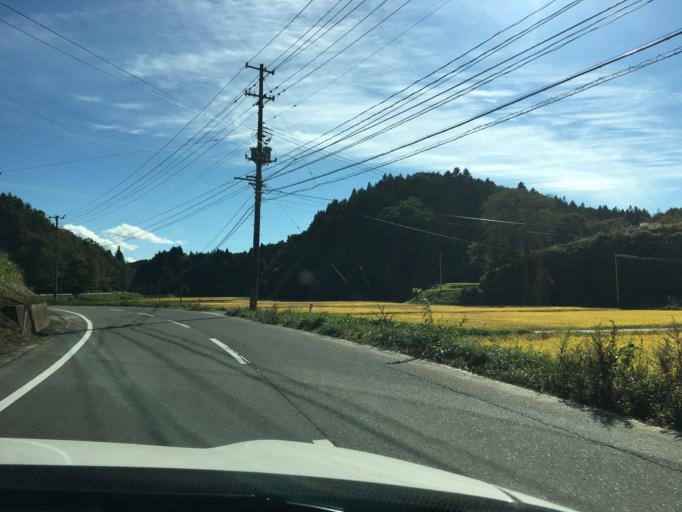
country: JP
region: Fukushima
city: Ishikawa
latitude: 37.2150
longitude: 140.5813
